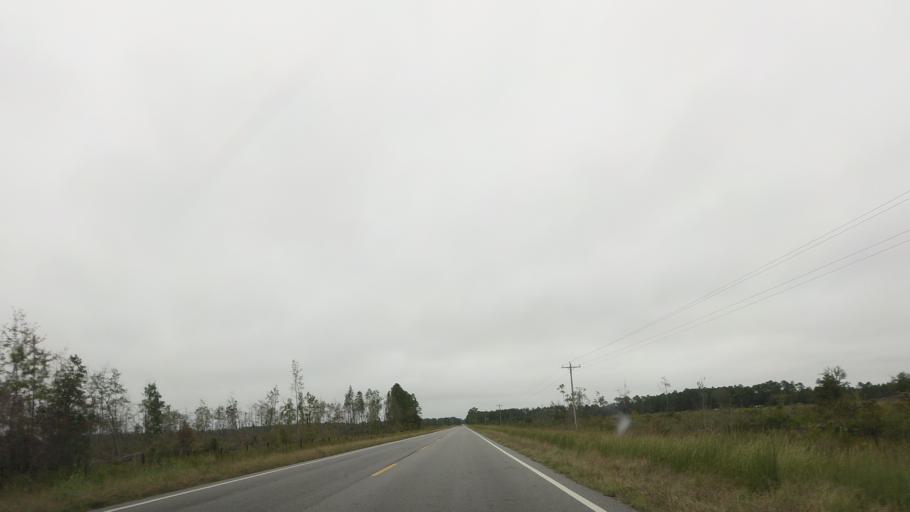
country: US
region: Georgia
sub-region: Berrien County
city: Enigma
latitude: 31.3582
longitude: -83.2275
